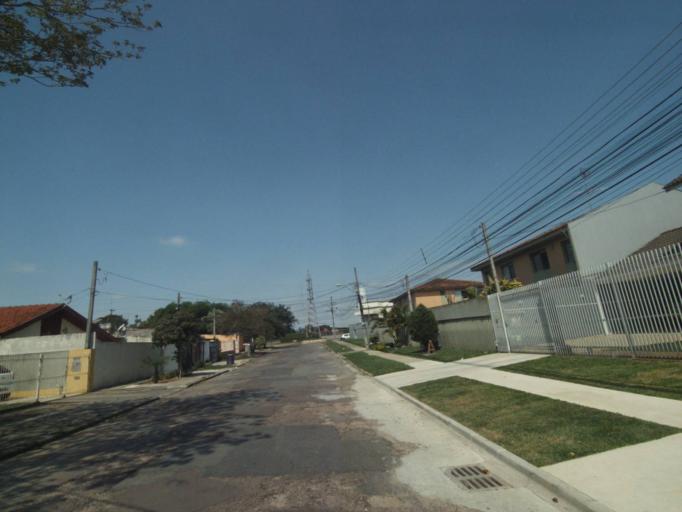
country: BR
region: Parana
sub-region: Curitiba
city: Curitiba
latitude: -25.4793
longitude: -49.3206
